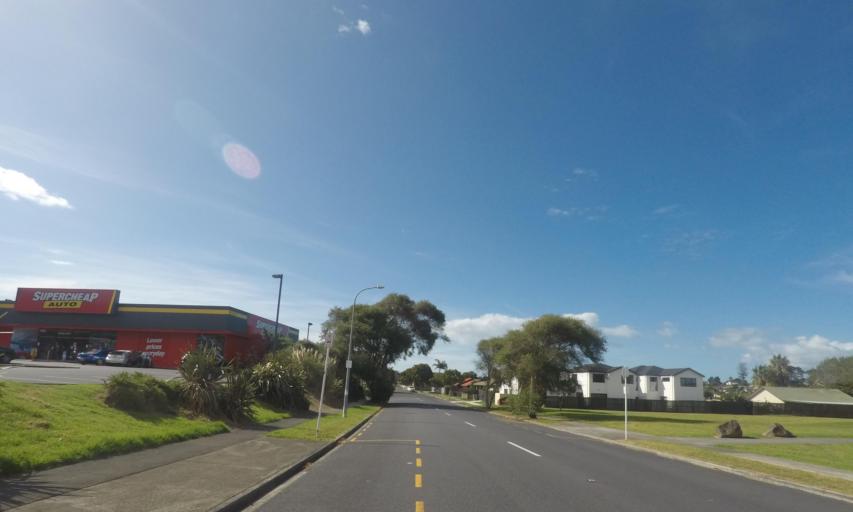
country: NZ
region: Auckland
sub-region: Auckland
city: Pakuranga
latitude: -36.9264
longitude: 174.9016
